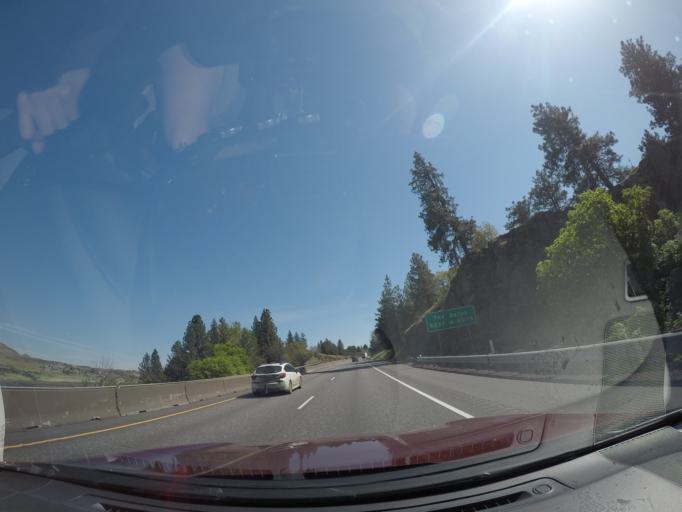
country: US
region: Oregon
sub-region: Wasco County
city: Chenoweth
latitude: 45.6582
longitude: -121.2149
